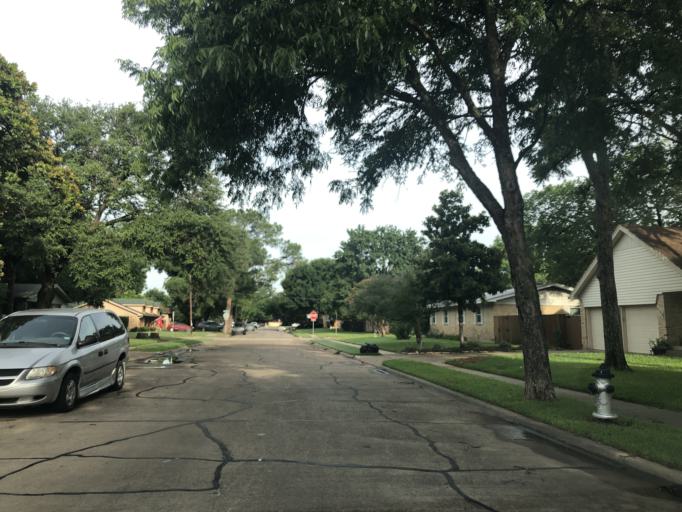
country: US
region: Texas
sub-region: Dallas County
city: Irving
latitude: 32.8035
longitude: -96.9823
